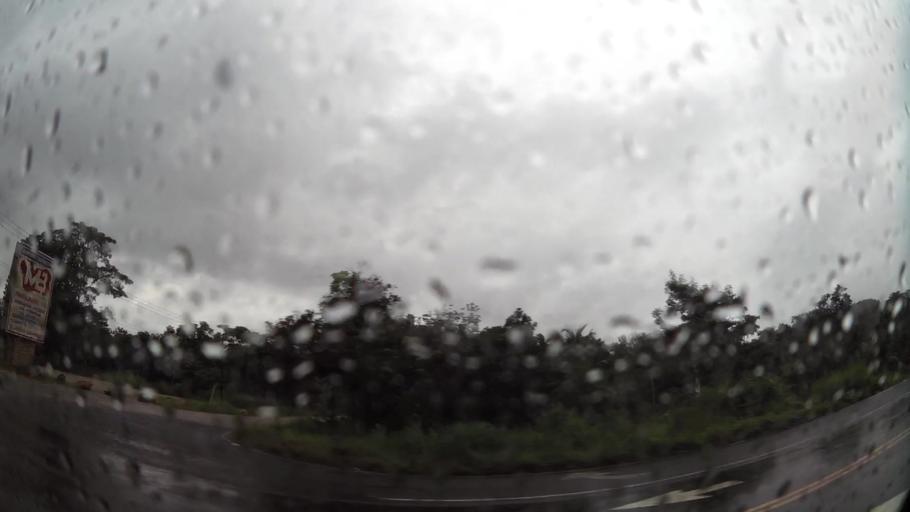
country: PA
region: Colon
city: Quebrada Bonita Adentro
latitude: 9.2854
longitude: -79.7157
